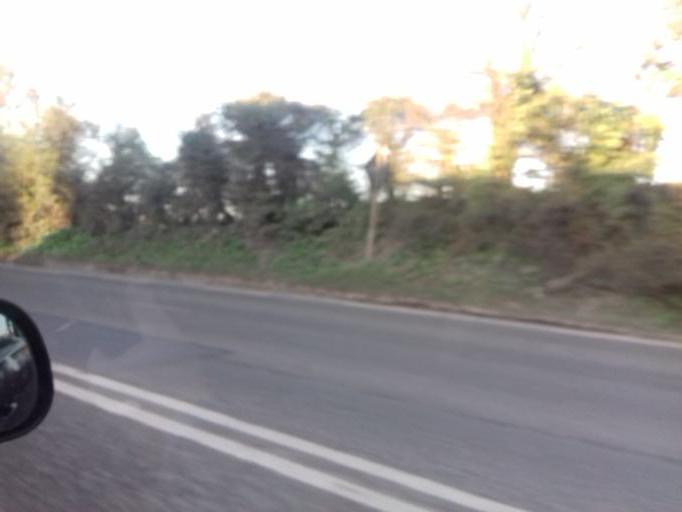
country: IE
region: Leinster
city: Lusk
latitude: 53.4965
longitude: -6.1940
